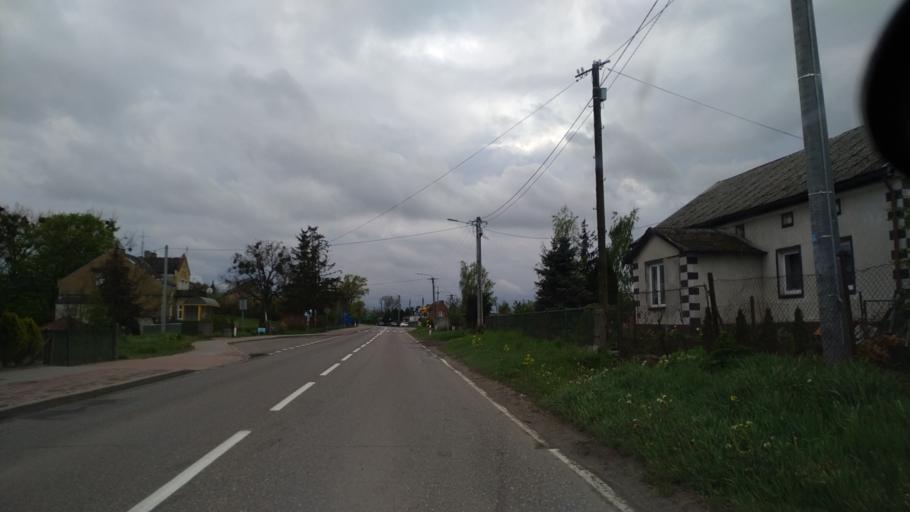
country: PL
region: Pomeranian Voivodeship
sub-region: Powiat kwidzynski
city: Kwidzyn
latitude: 53.7595
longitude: 18.9433
